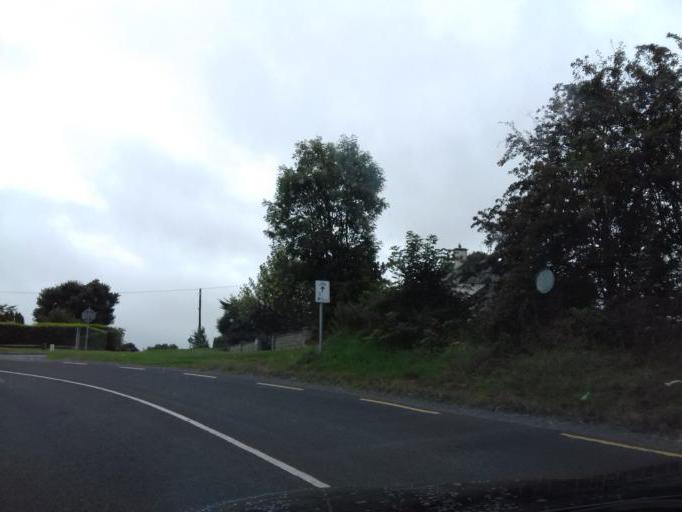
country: IE
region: Leinster
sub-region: County Carlow
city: Bagenalstown
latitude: 52.6274
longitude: -7.0123
